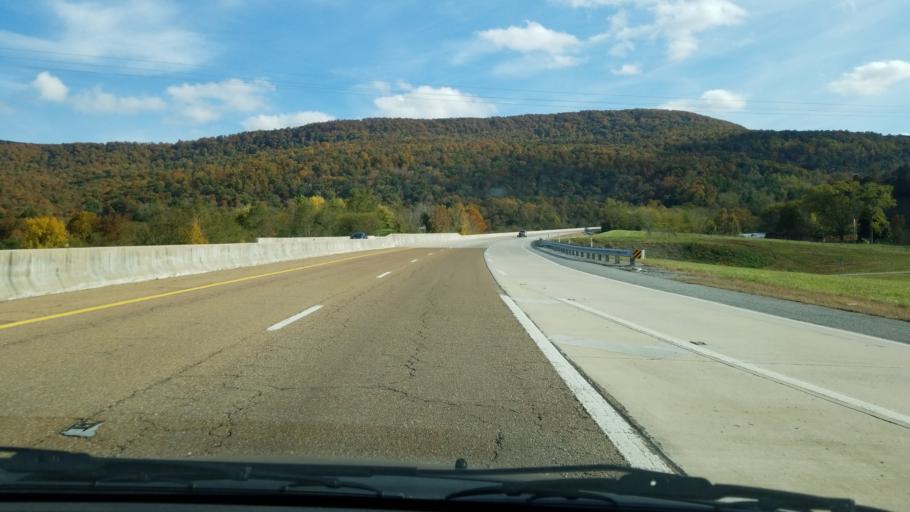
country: US
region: Tennessee
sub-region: Sequatchie County
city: Dunlap
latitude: 35.3899
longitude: -85.3336
